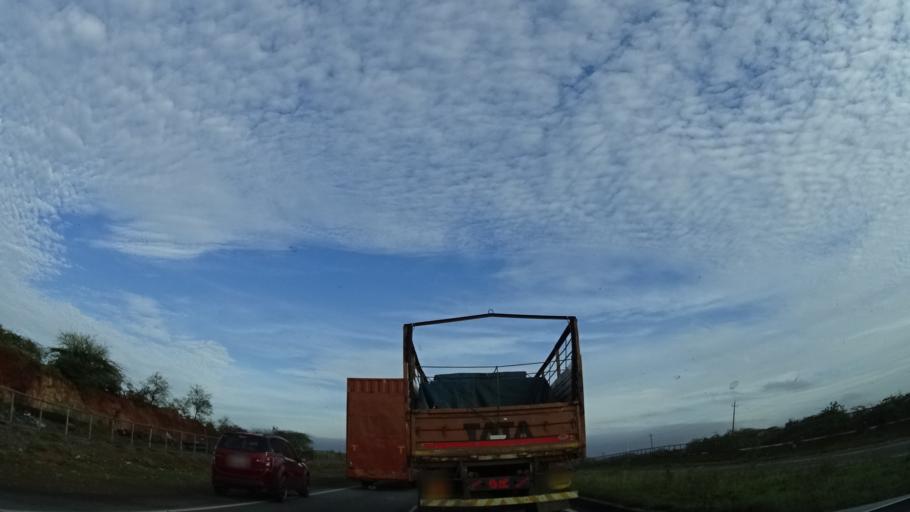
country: IN
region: Karnataka
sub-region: Chitradurga
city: Chitradurga
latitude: 14.1849
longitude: 76.4593
